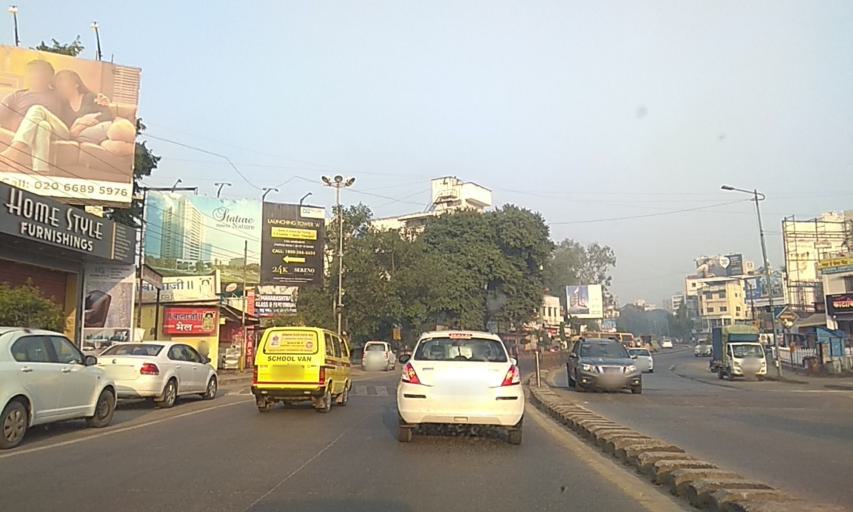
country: IN
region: Maharashtra
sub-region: Pune Division
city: Pimpri
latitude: 18.5617
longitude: 73.7844
